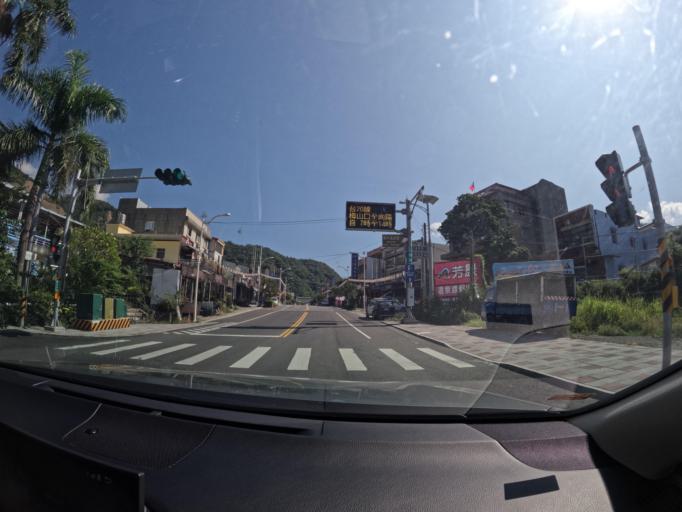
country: TW
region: Taiwan
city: Yujing
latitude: 23.1076
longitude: 120.6983
